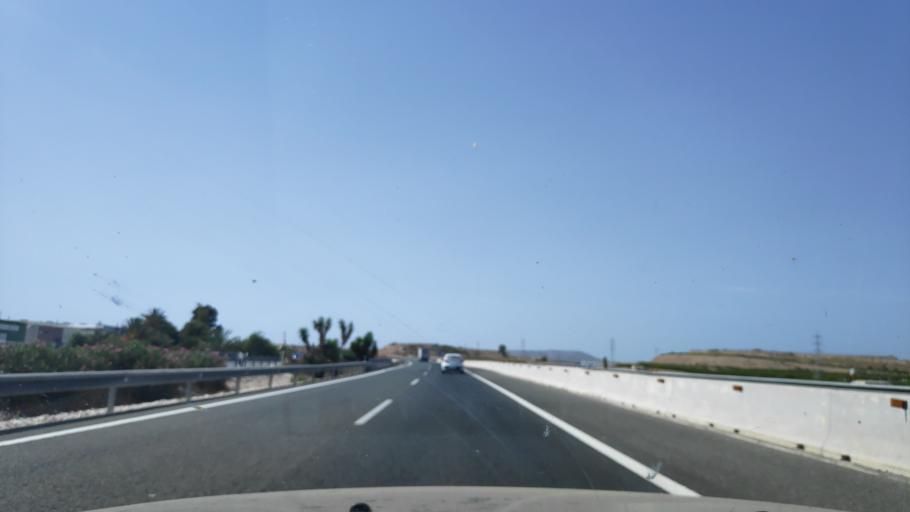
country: ES
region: Murcia
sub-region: Murcia
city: Blanca
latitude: 38.1924
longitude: -1.3309
